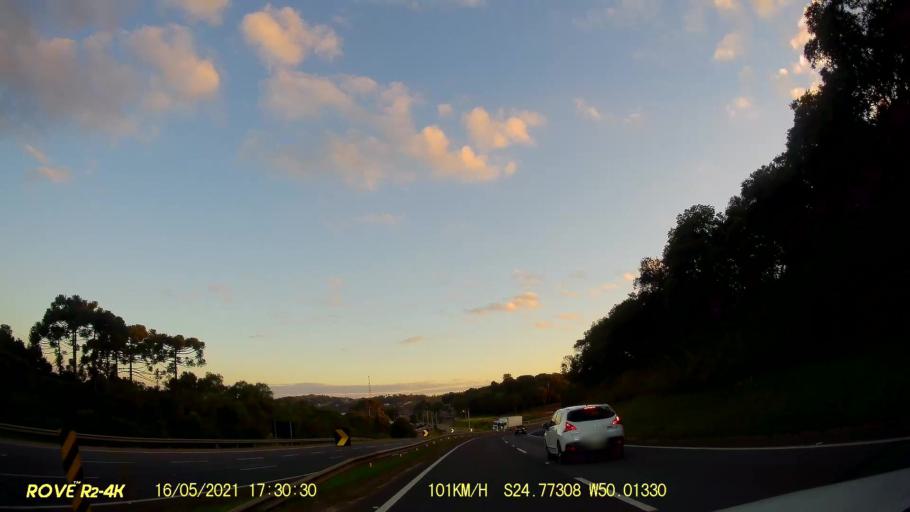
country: BR
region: Parana
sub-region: Castro
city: Castro
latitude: -24.7743
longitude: -50.0137
